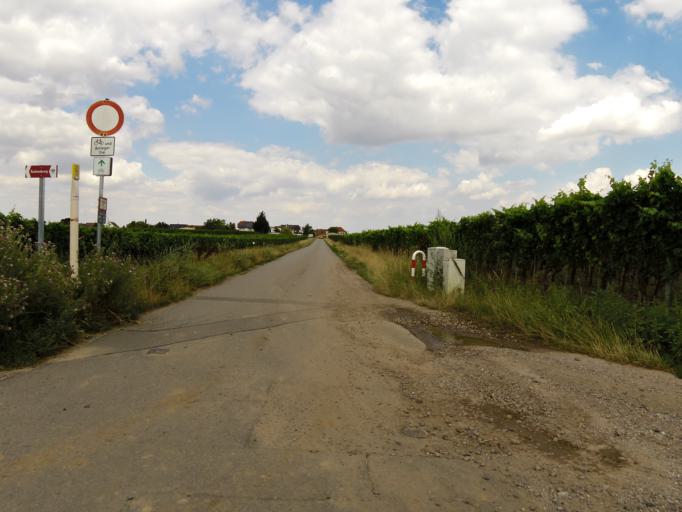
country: DE
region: Rheinland-Pfalz
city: Ellerstadt
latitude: 49.4570
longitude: 8.2599
